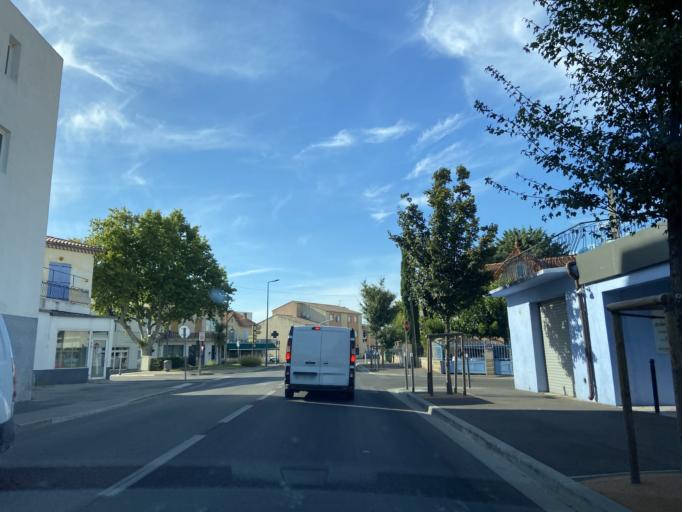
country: FR
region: Provence-Alpes-Cote d'Azur
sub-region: Departement des Bouches-du-Rhone
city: Miramas
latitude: 43.5853
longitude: 5.0027
